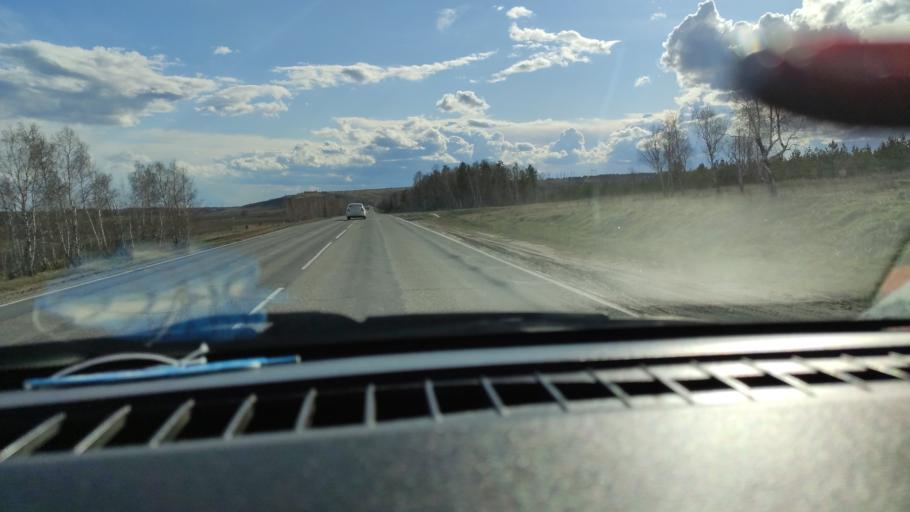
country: RU
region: Saratov
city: Sennoy
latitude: 52.1070
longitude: 46.8235
